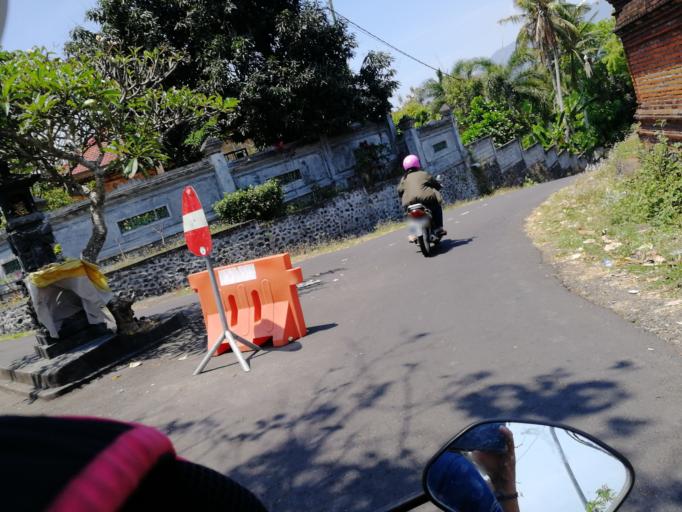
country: ID
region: Bali
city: Banjar Timbrah
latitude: -8.4675
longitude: 115.5915
